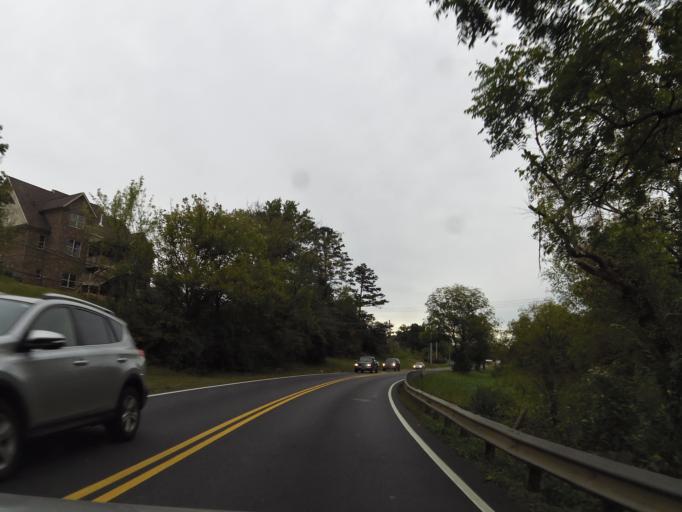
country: US
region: Tennessee
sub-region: Blount County
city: Louisville
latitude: 35.8785
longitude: -84.0412
